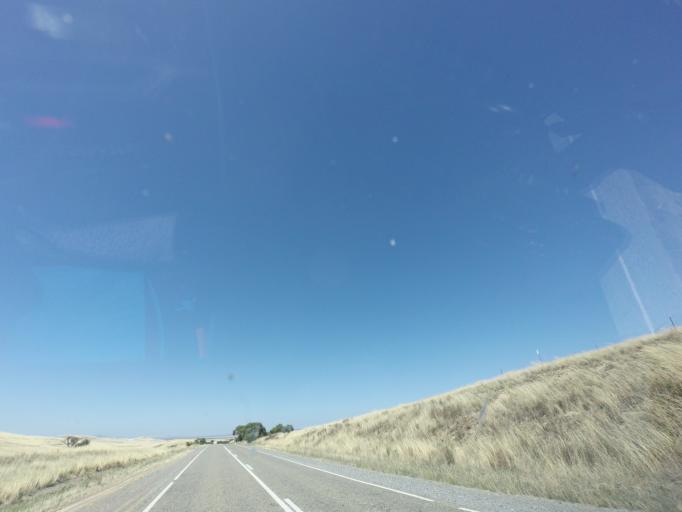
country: AU
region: South Australia
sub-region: Peterborough
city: Peterborough
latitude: -32.7426
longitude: 138.5742
